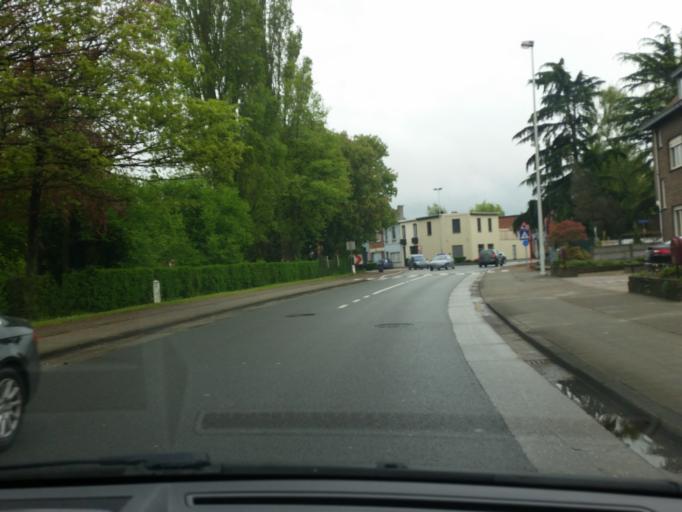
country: BE
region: Flanders
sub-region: Provincie Antwerpen
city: Borsbeek
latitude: 51.1892
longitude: 4.4879
